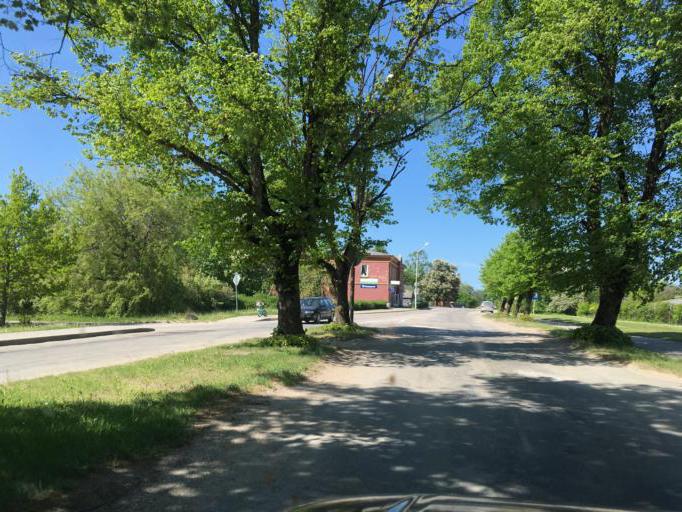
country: LV
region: Dundaga
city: Dundaga
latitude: 57.5079
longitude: 22.3497
